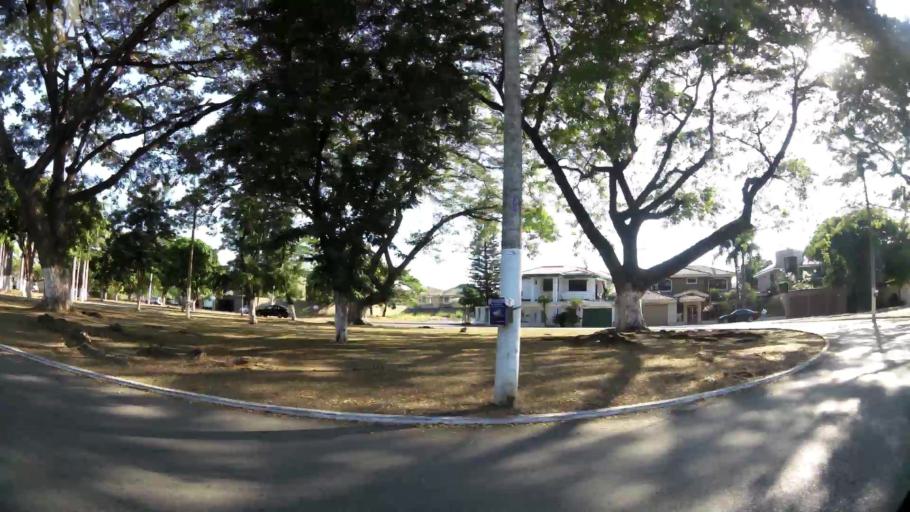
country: EC
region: Guayas
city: Santa Lucia
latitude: -2.1918
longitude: -79.9673
